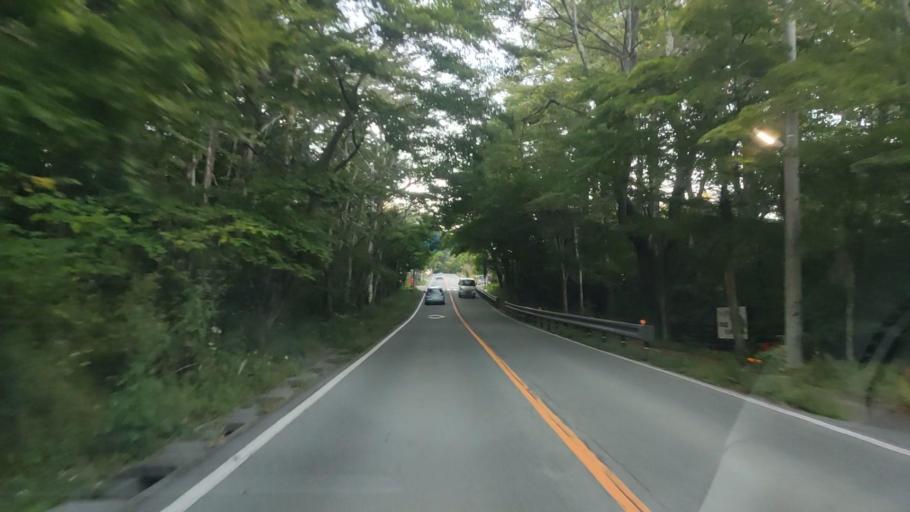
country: JP
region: Nagano
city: Komoro
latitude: 36.3713
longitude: 138.5876
